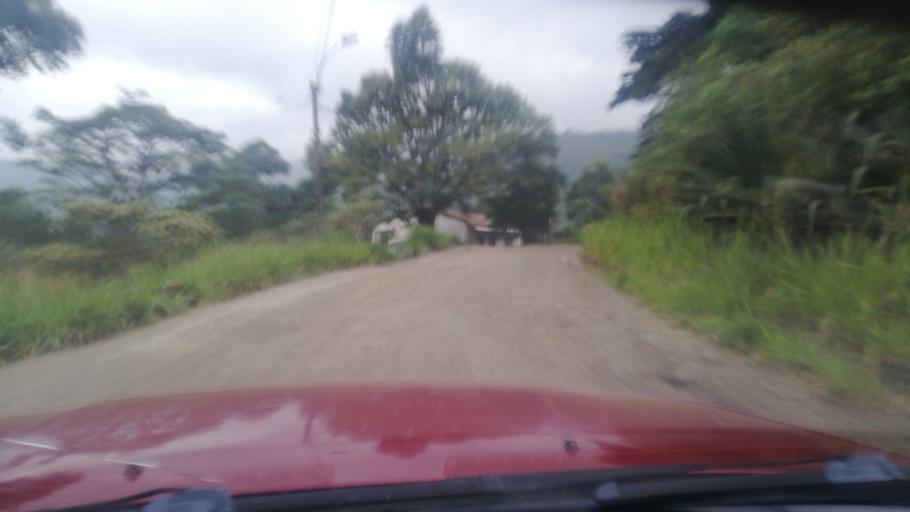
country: CO
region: Valle del Cauca
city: Cali
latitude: 3.4925
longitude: -76.5478
